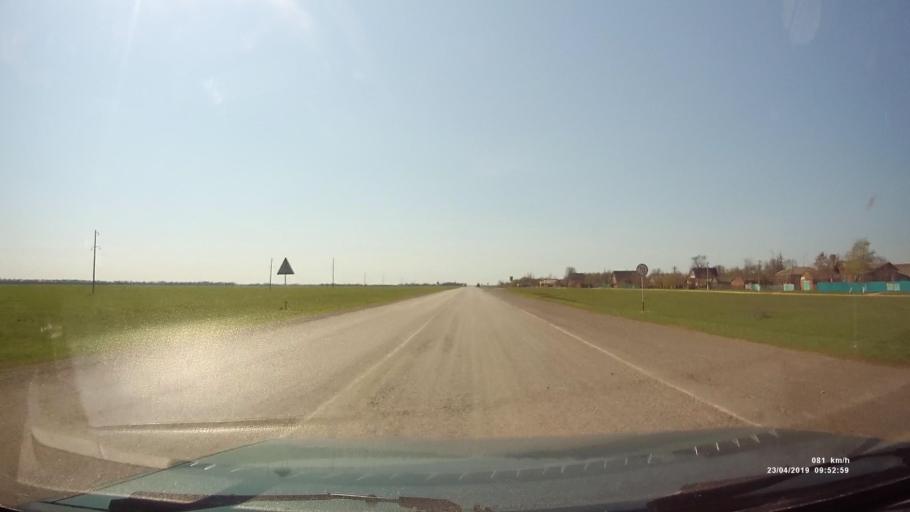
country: RU
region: Rostov
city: Orlovskiy
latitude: 46.8381
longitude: 42.0483
